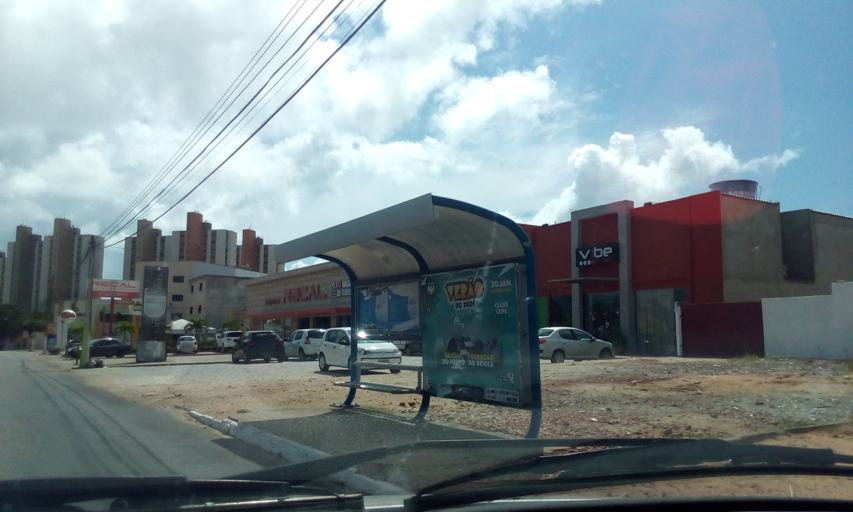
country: BR
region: Rio Grande do Norte
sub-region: Parnamirim
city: Parnamirim
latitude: -5.8957
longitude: -35.1967
